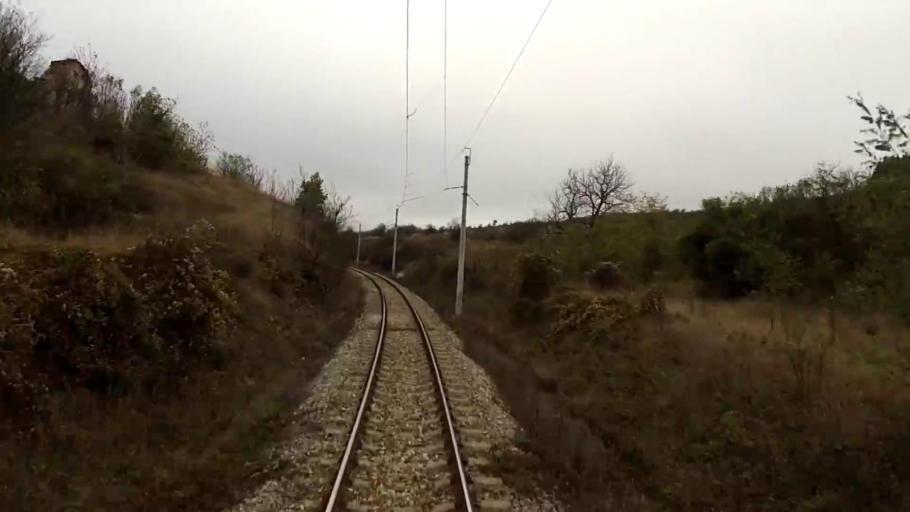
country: BG
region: Sofiya
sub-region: Obshtina Dragoman
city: Dragoman
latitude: 42.9414
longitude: 22.9011
